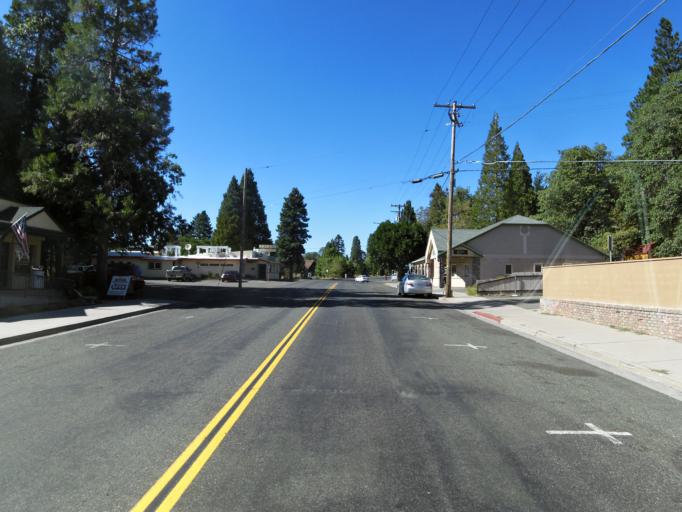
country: US
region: California
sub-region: Siskiyou County
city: Mount Shasta
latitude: 41.3054
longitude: -122.3100
